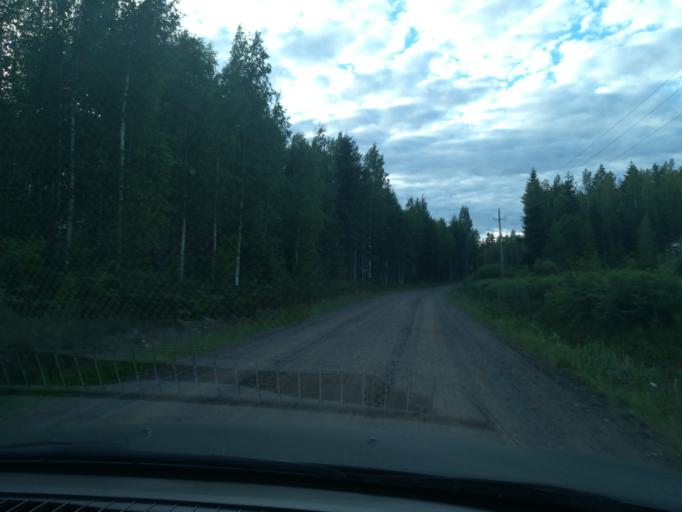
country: FI
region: Southern Savonia
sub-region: Mikkeli
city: Puumala
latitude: 61.6066
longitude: 28.1464
